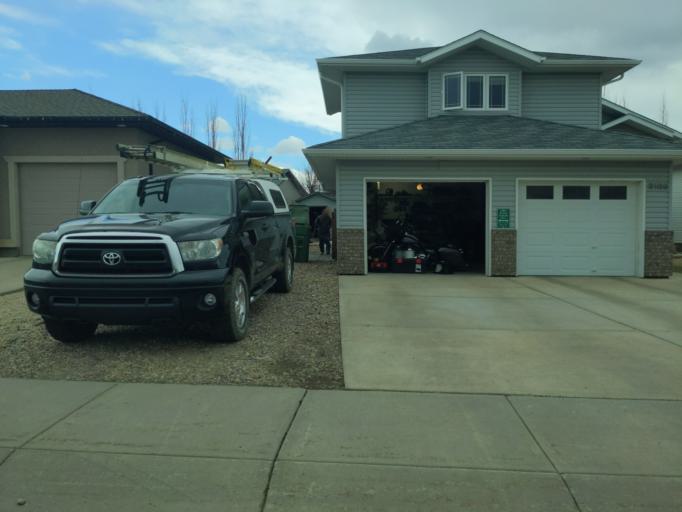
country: CA
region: Saskatchewan
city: Lloydminster
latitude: 53.2669
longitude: -110.0423
